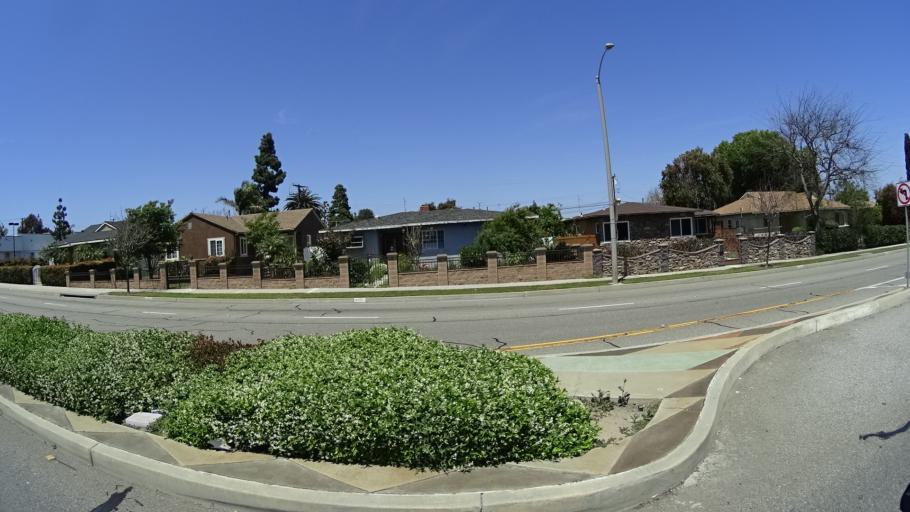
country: US
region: California
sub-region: Los Angeles County
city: Lawndale
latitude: 33.8734
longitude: -118.3513
